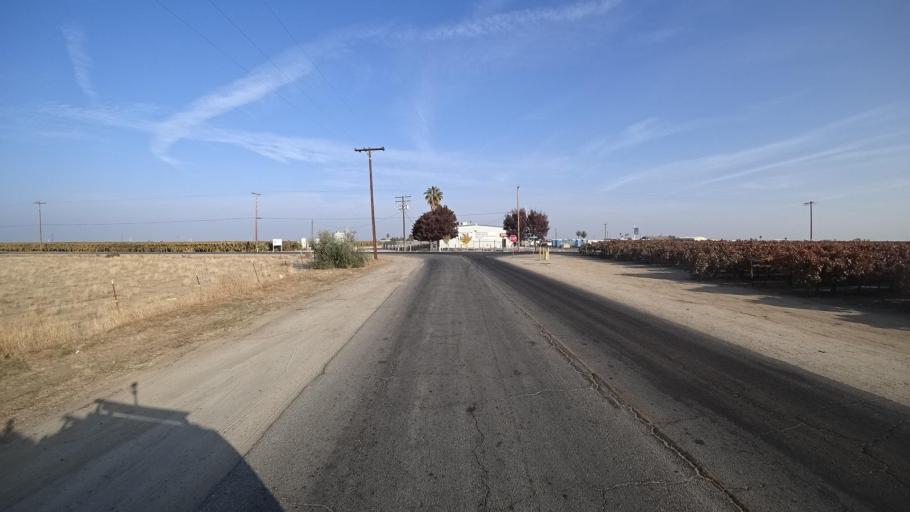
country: US
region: California
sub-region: Kern County
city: Delano
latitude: 35.7900
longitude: -119.1875
